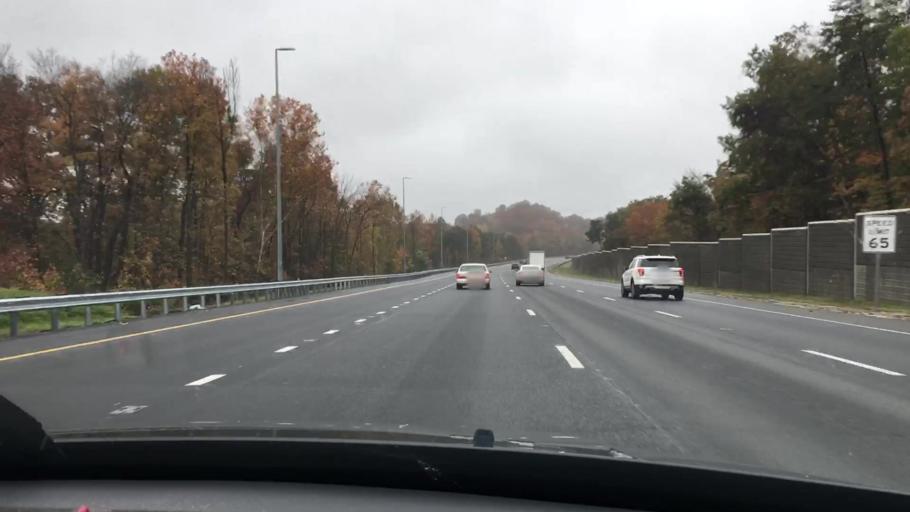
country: US
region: Virginia
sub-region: Stafford County
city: Aquia Harbour
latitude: 38.4552
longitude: -77.4090
